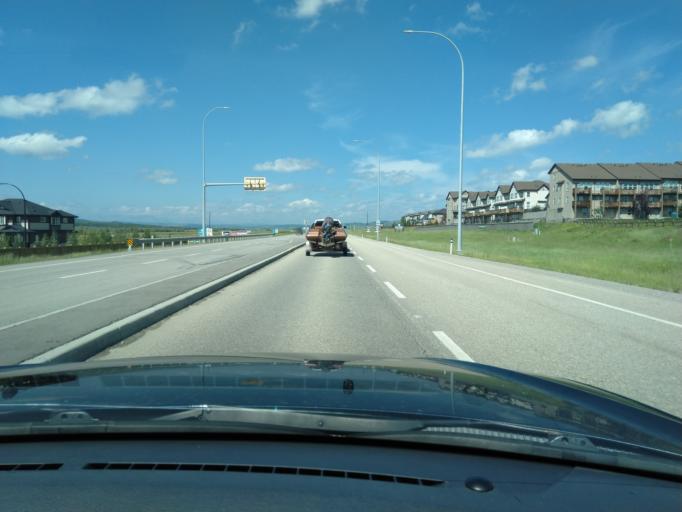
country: CA
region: Alberta
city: Cochrane
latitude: 51.2041
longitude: -114.5051
